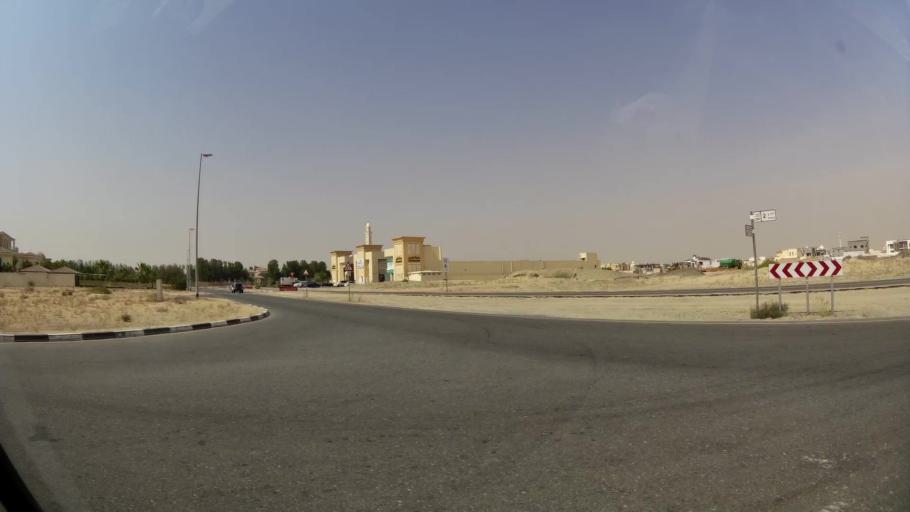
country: AE
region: Ash Shariqah
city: Sharjah
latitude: 25.2480
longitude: 55.4789
